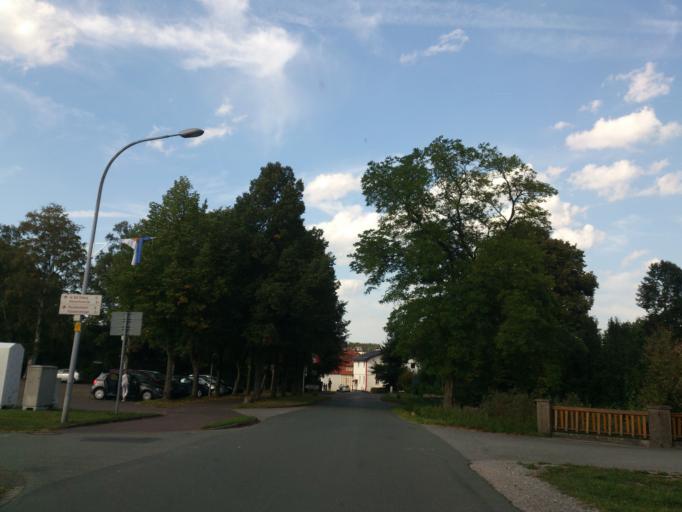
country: DE
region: North Rhine-Westphalia
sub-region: Regierungsbezirk Detmold
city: Willebadessen
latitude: 51.6237
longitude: 9.0315
